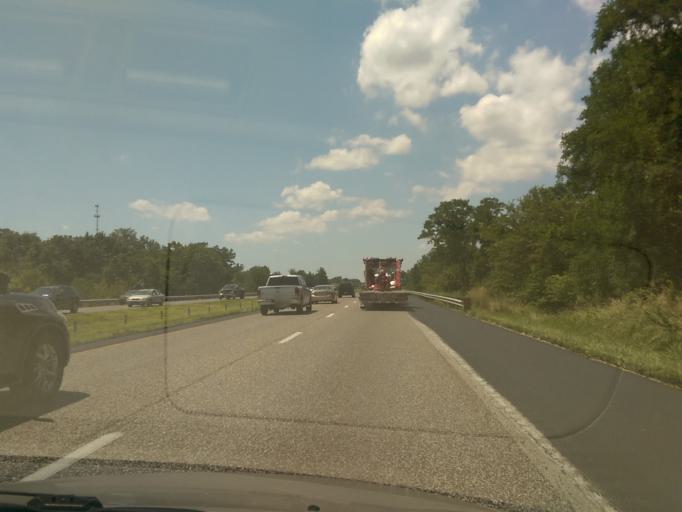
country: US
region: Missouri
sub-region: Cooper County
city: Boonville
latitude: 38.9400
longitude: -92.5876
